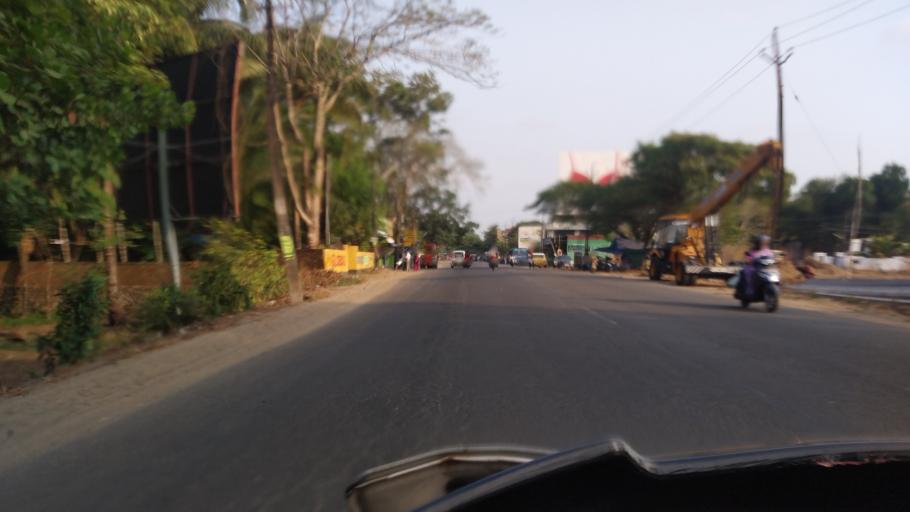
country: IN
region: Kerala
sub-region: Thrissur District
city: Thanniyam
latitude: 10.4232
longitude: 76.1034
